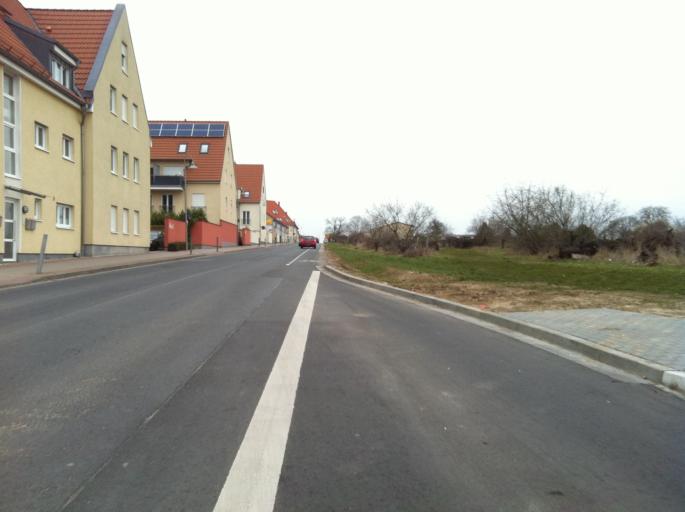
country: DE
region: Rheinland-Pfalz
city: Wackernheim
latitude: 49.9745
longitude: 8.1196
